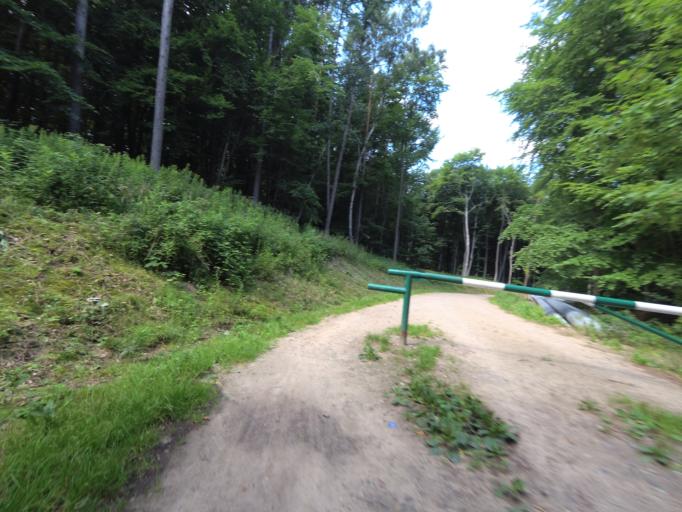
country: PL
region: Pomeranian Voivodeship
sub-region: Gdynia
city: Wielki Kack
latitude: 54.4787
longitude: 18.5013
